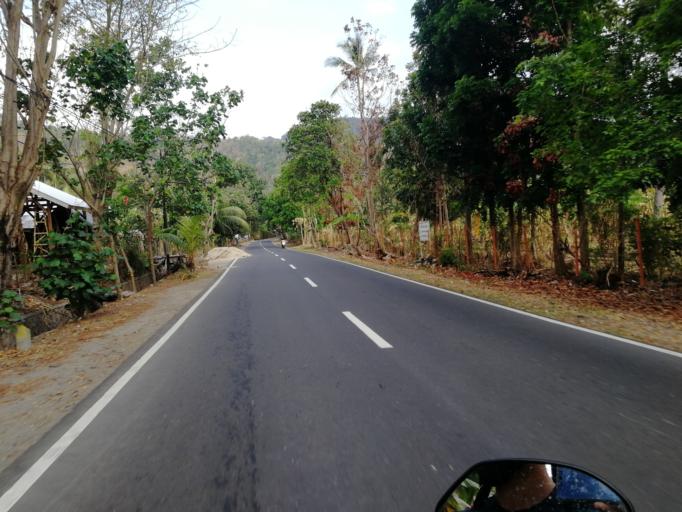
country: ID
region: West Nusa Tenggara
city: Karangsubagan
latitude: -8.4498
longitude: 116.0383
